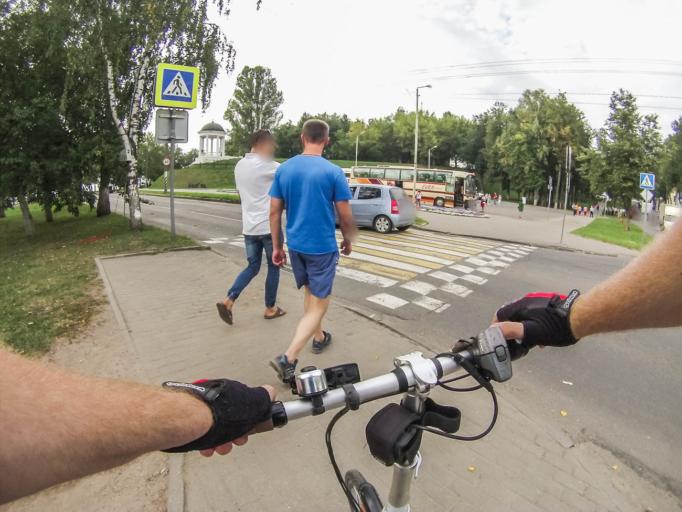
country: RU
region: Kostroma
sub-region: Kostromskoy Rayon
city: Kostroma
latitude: 57.7615
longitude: 40.9295
